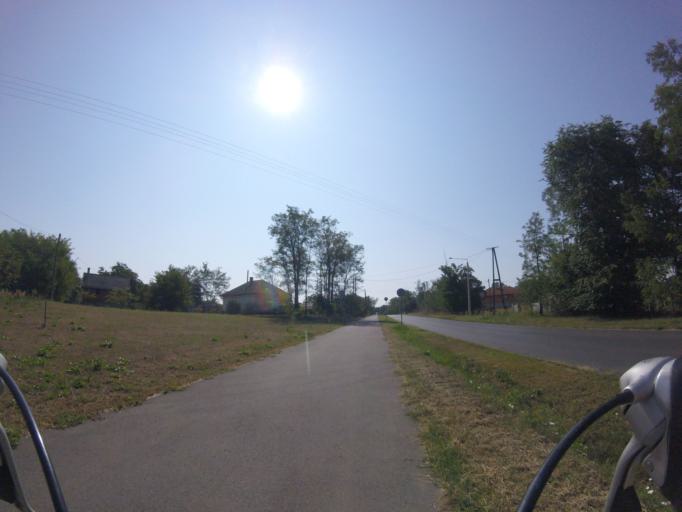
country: HU
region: Szabolcs-Szatmar-Bereg
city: Kotaj
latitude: 48.0116
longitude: 21.6916
